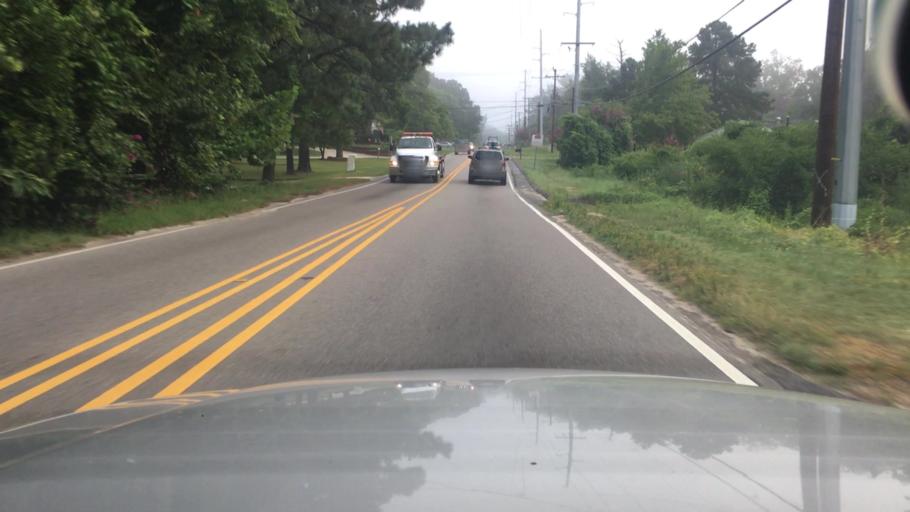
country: US
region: North Carolina
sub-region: Cumberland County
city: Hope Mills
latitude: 35.0165
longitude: -78.9401
